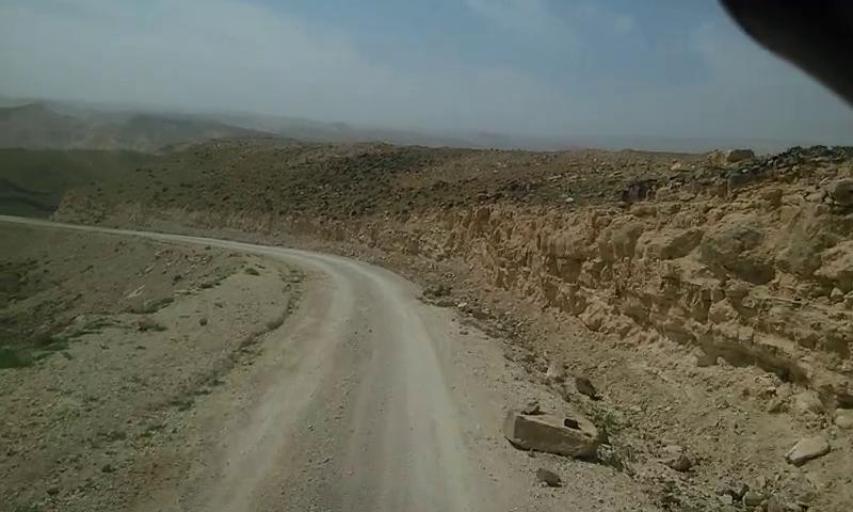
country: PS
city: `Arab ar Rashaydah
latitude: 31.5174
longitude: 35.2943
